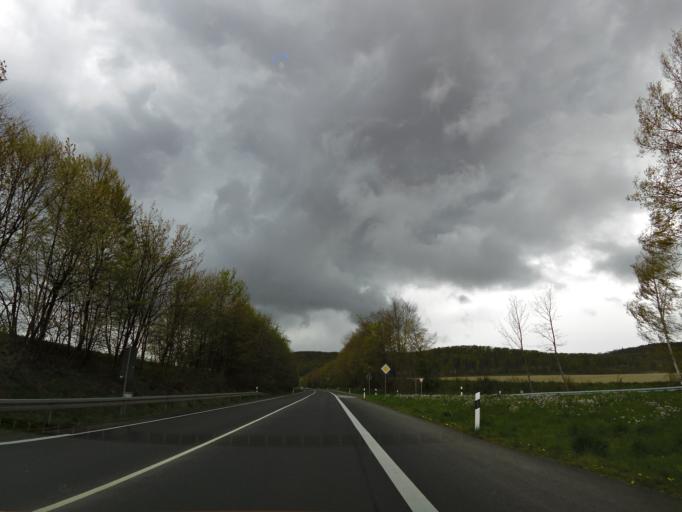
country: DE
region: Lower Saxony
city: Hahausen
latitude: 51.9566
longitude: 10.2323
